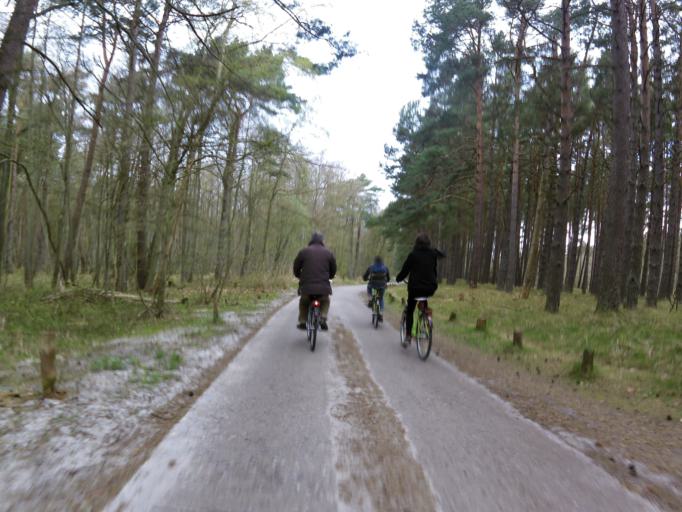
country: DE
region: Mecklenburg-Vorpommern
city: Ostseebad Prerow
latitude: 54.4614
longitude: 12.5310
